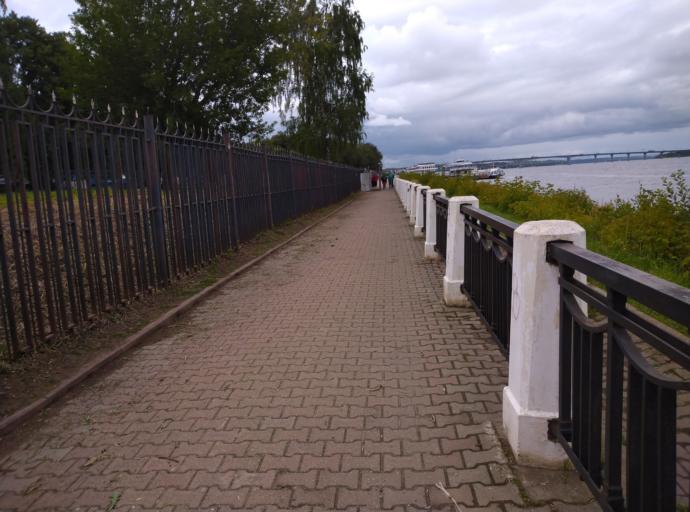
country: RU
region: Kostroma
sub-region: Kostromskoy Rayon
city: Kostroma
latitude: 57.7637
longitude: 40.9229
